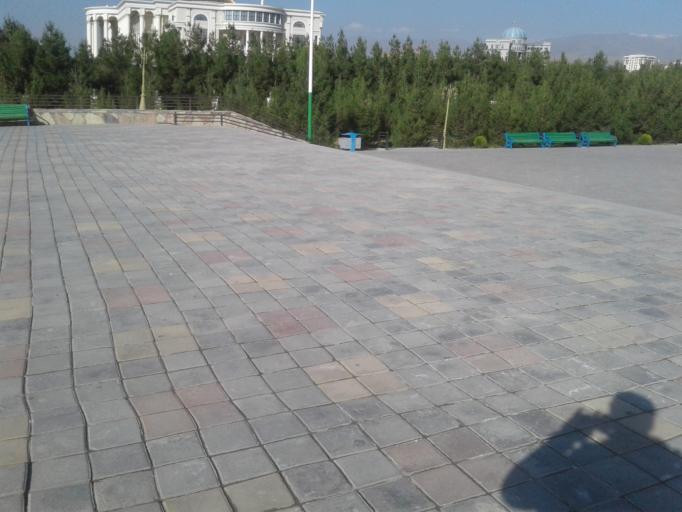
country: TJ
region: Dushanbe
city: Dushanbe
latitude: 38.5738
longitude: 68.7780
